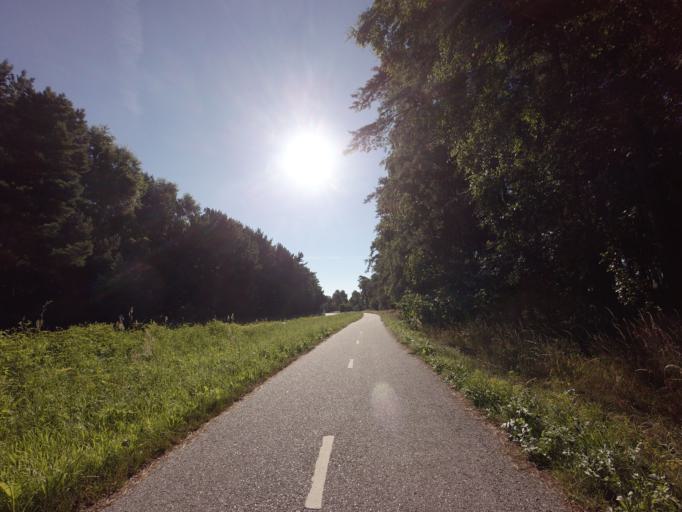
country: SE
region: Skane
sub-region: Ystads Kommun
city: Ystad
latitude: 55.4256
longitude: 13.7693
